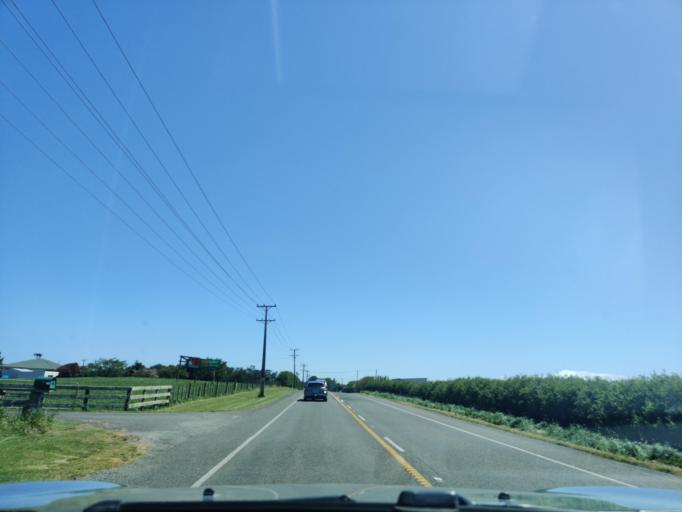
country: NZ
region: Taranaki
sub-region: South Taranaki District
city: Hawera
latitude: -39.6047
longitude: 174.3132
